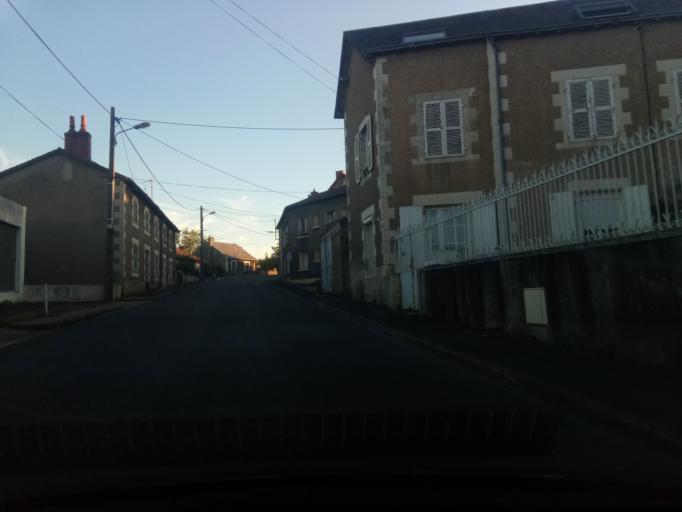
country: FR
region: Poitou-Charentes
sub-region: Departement de la Vienne
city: Montmorillon
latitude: 46.4217
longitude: 0.8661
